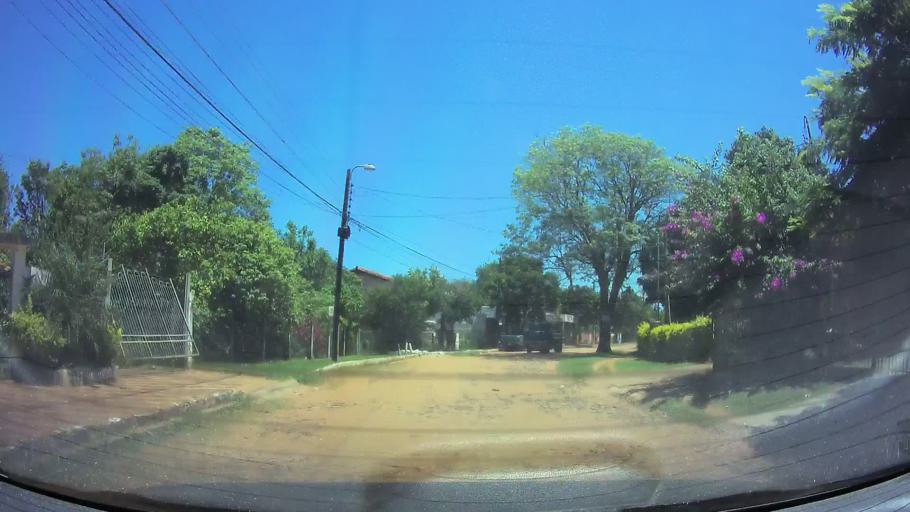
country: PY
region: Central
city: Limpio
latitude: -25.2447
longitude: -57.4868
